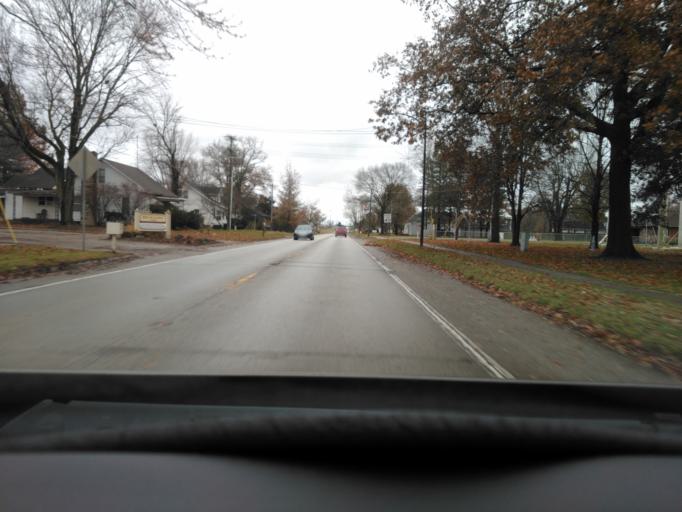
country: US
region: Illinois
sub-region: Effingham County
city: Altamont
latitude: 39.0530
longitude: -88.7480
